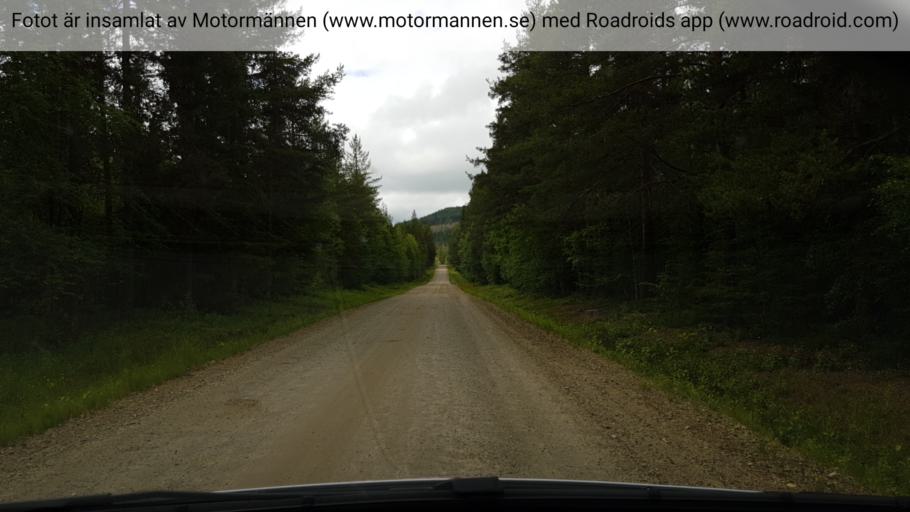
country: SE
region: Vaesterbotten
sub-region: Norsjo Kommun
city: Norsjoe
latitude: 64.6030
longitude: 19.1573
